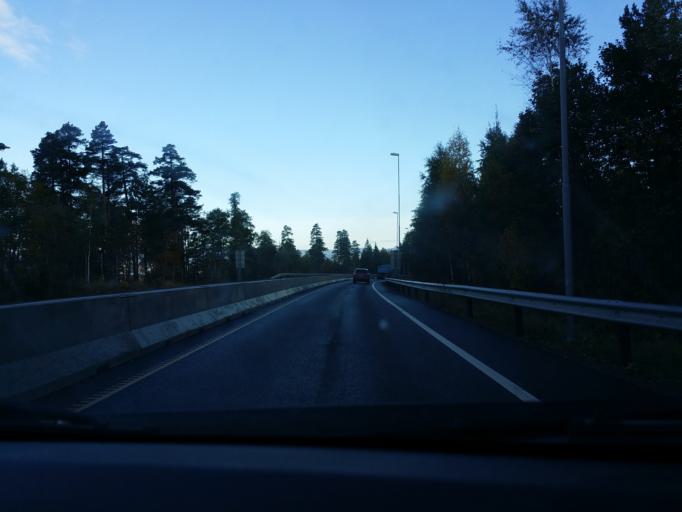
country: NO
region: Buskerud
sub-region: Hole
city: Vik
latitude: 60.0348
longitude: 10.2713
